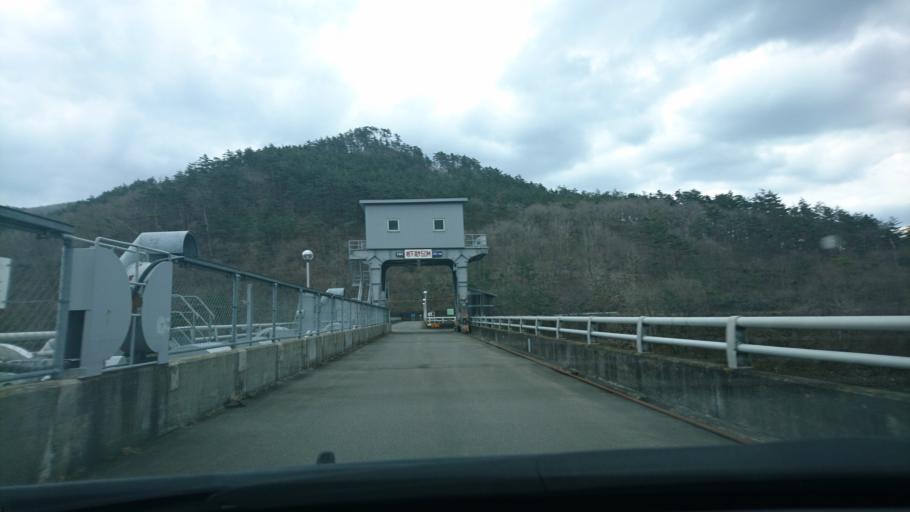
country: JP
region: Iwate
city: Hanamaki
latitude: 39.3431
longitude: 141.3186
